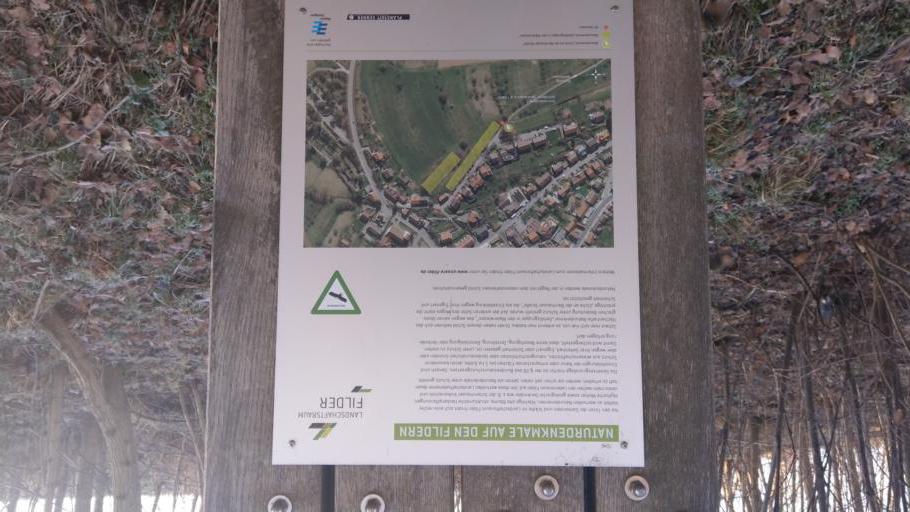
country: DE
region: Baden-Wuerttemberg
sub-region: Regierungsbezirk Stuttgart
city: Ostfildern
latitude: 48.7057
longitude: 9.2624
